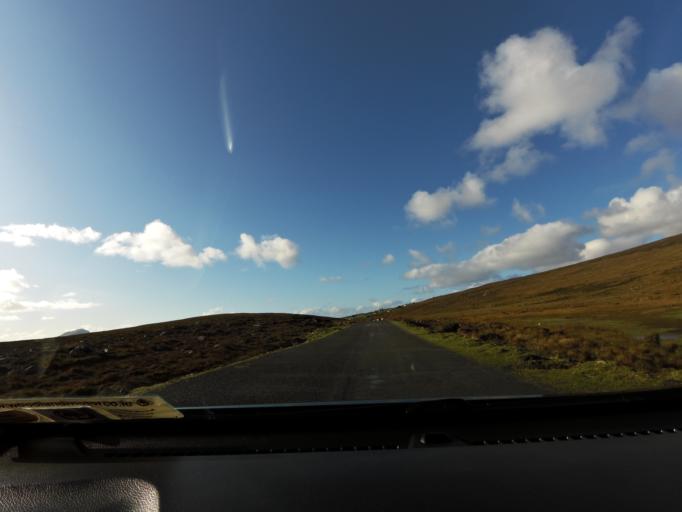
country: IE
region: Connaught
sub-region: Maigh Eo
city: Westport
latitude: 53.8675
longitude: -9.8787
